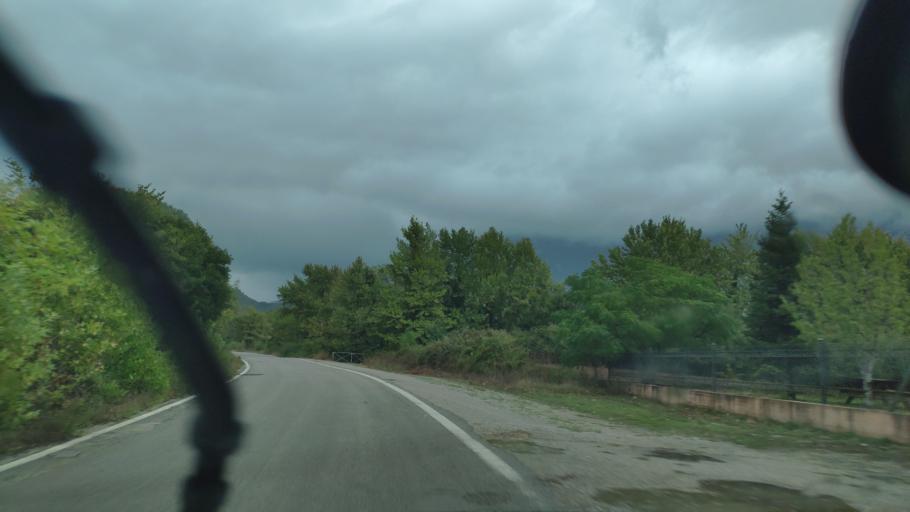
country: GR
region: West Greece
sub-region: Nomos Aitolias kai Akarnanias
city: Krikellos
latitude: 39.0104
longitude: 21.3100
